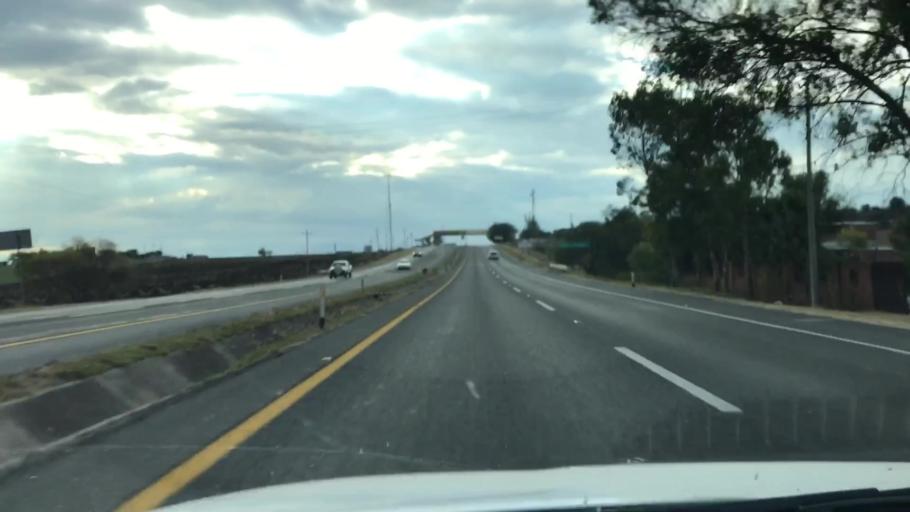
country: MX
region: Guanajuato
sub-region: Penjamo
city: Mezquite de Luna
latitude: 20.3799
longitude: -101.8312
